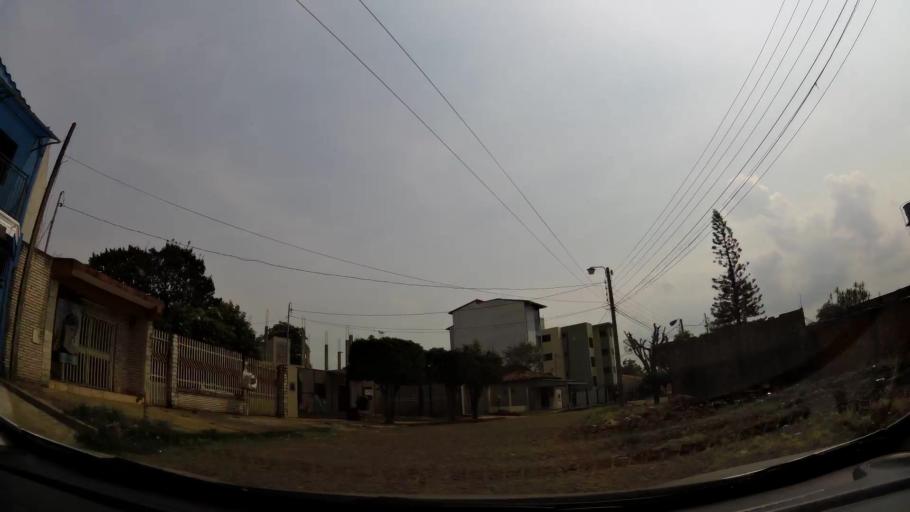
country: PY
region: Alto Parana
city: Presidente Franco
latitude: -25.5448
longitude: -54.6282
